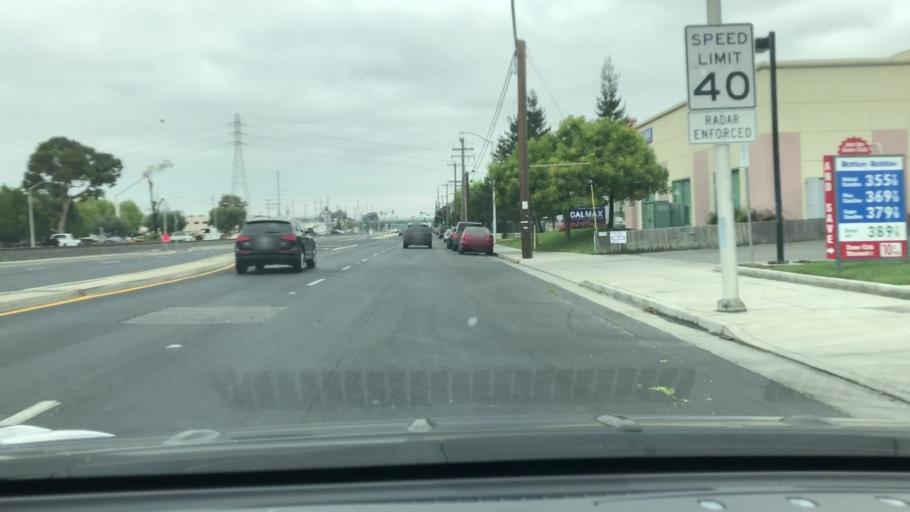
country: US
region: California
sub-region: Santa Clara County
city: Santa Clara
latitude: 37.3834
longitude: -121.9508
